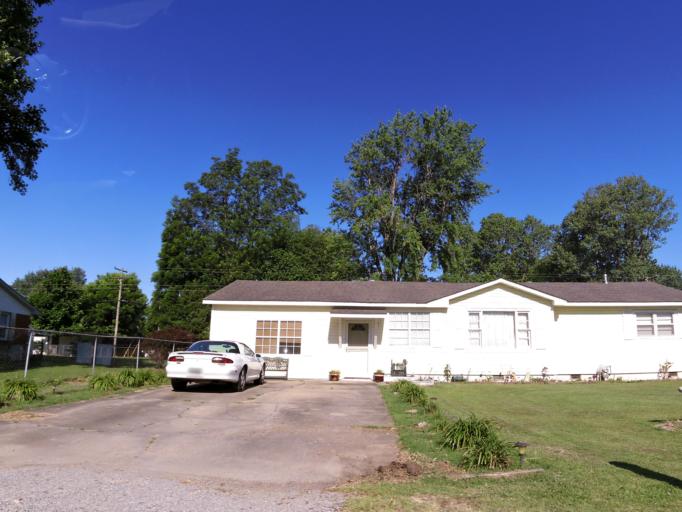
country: US
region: Arkansas
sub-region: Clay County
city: Corning
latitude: 36.4132
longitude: -90.6000
